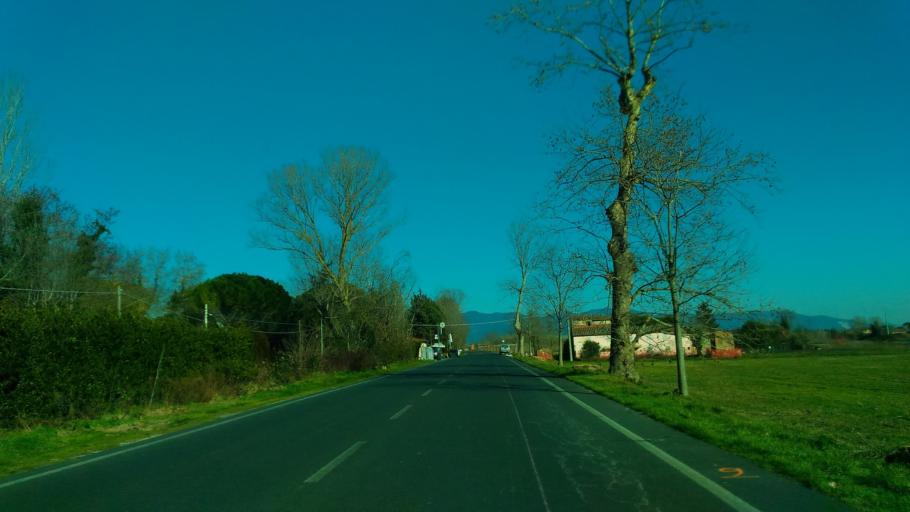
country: IT
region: Tuscany
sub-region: Province of Pisa
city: Marina di Pisa-Tirrenia-Calambrone
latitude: 43.6799
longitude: 10.3310
